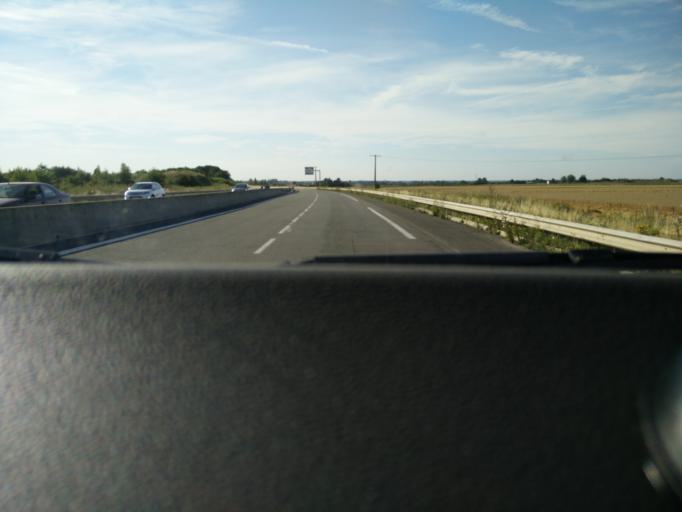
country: FR
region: Nord-Pas-de-Calais
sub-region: Departement du Nord
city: Abscon
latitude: 50.3392
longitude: 3.3183
